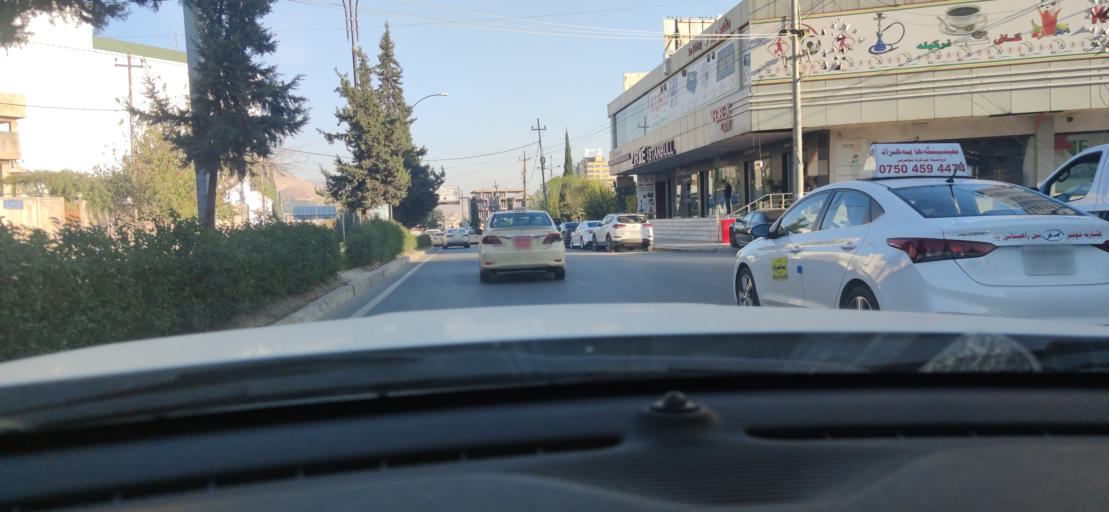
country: IQ
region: Dahuk
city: Dihok
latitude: 36.8666
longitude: 42.9814
